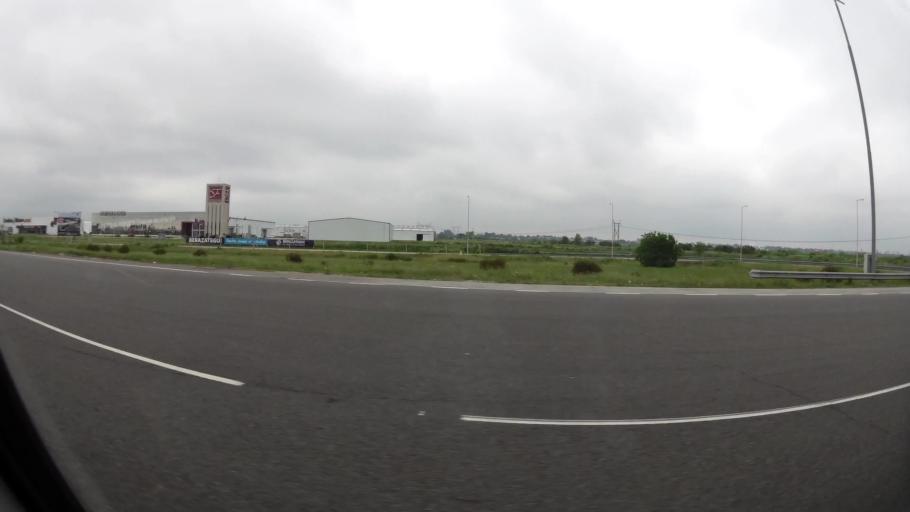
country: AR
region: Buenos Aires
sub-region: Partido de Quilmes
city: Quilmes
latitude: -34.7730
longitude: -58.1648
